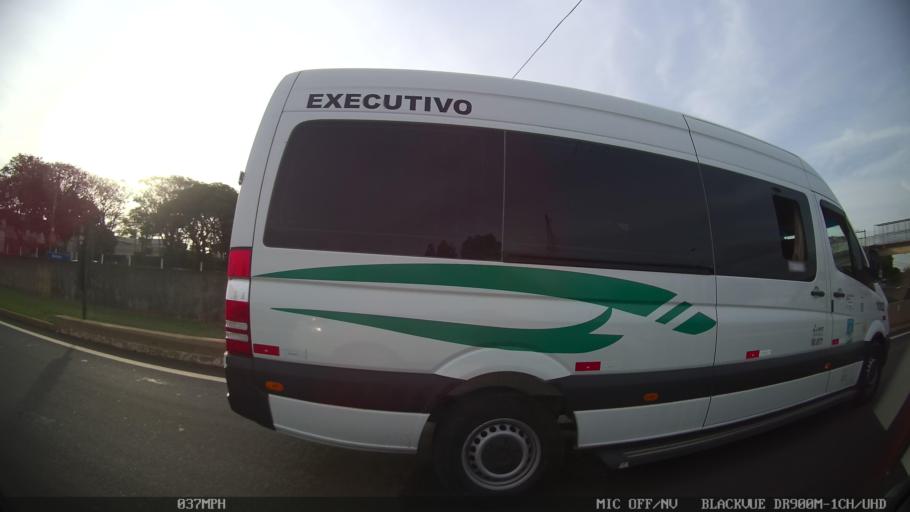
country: BR
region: Sao Paulo
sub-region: Limeira
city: Limeira
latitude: -22.5632
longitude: -47.4243
